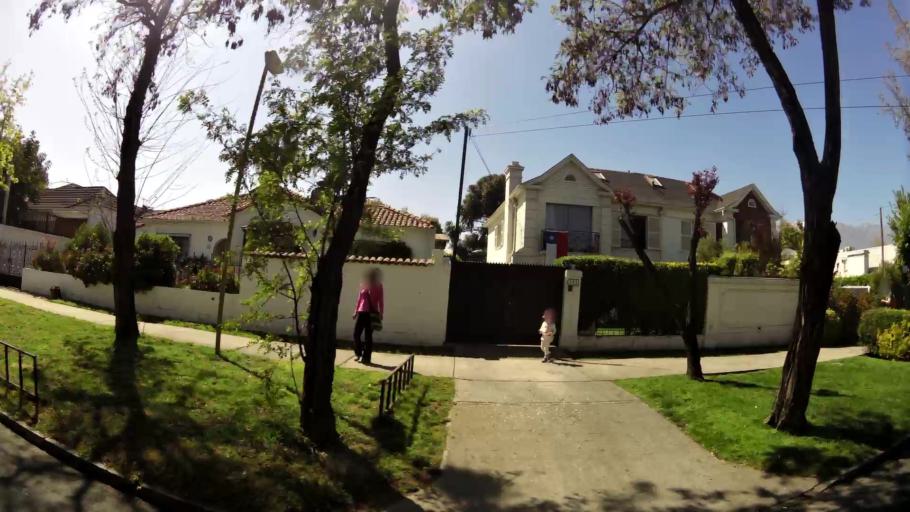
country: CL
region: Santiago Metropolitan
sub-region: Provincia de Santiago
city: Villa Presidente Frei, Nunoa, Santiago, Chile
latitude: -33.4142
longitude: -70.5729
